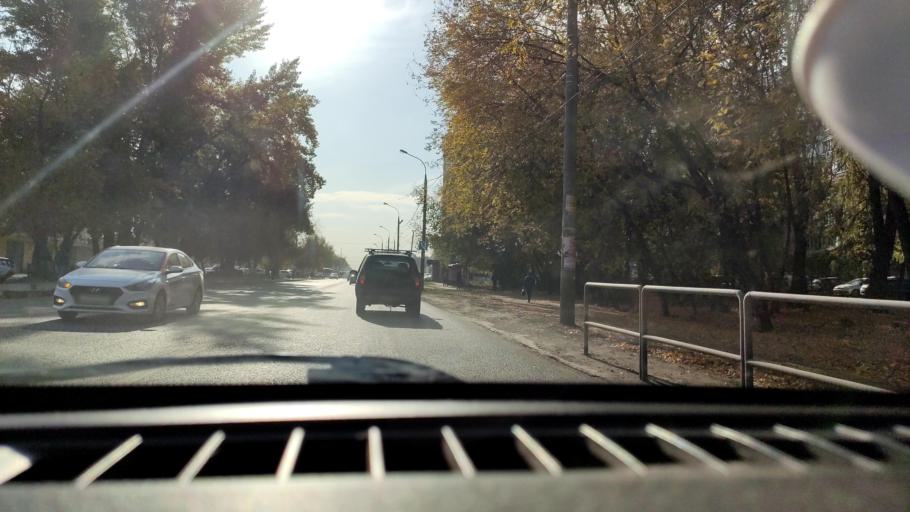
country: RU
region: Samara
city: Samara
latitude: 53.2234
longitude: 50.2005
